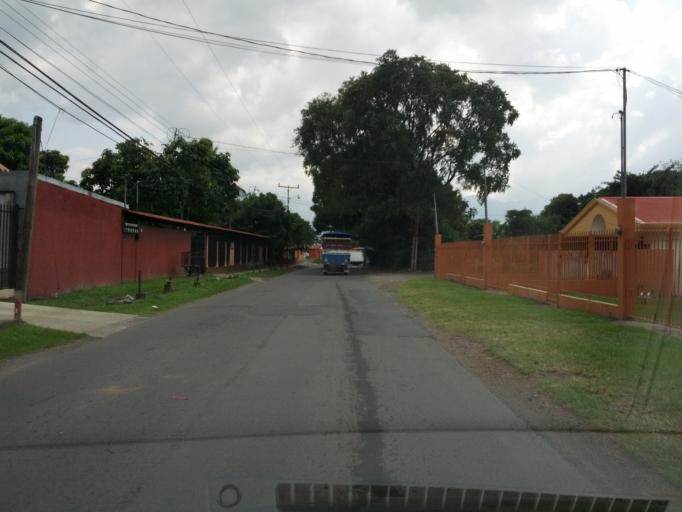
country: CR
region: Alajuela
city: Alajuela
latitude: 9.9856
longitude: -84.2226
